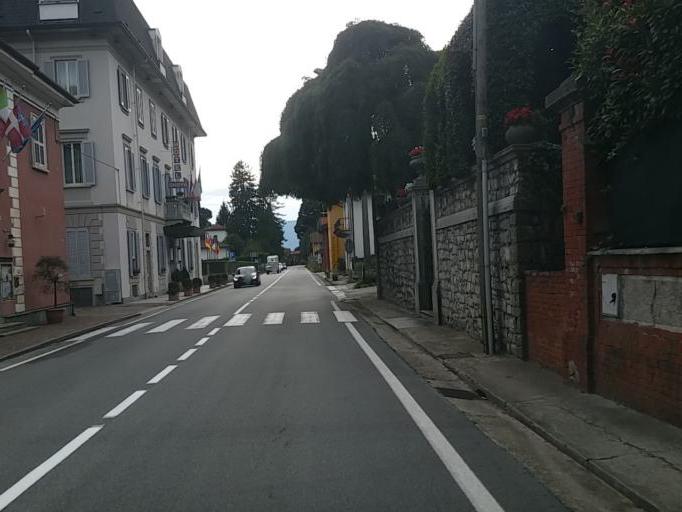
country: IT
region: Piedmont
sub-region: Provincia Verbano-Cusio-Ossola
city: Ghiffa
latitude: 45.9565
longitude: 8.6172
